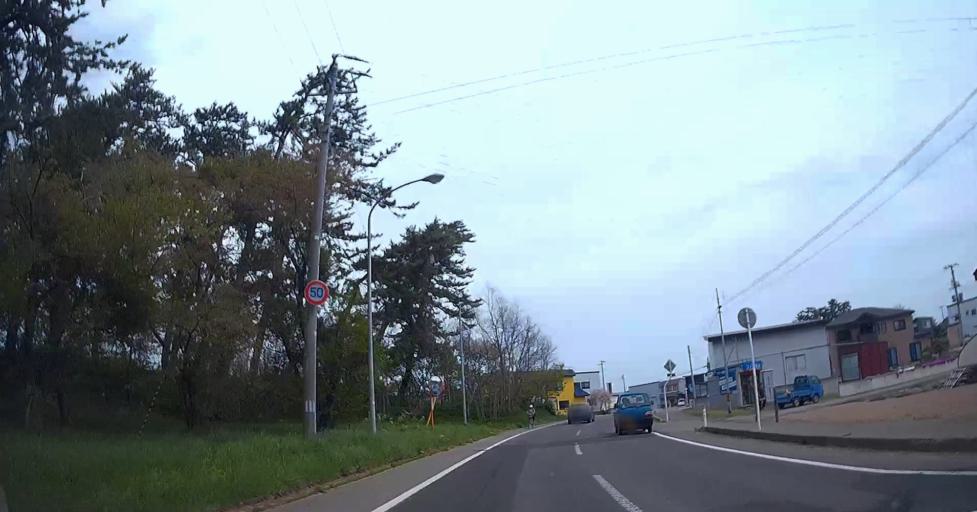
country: JP
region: Aomori
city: Shimokizukuri
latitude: 40.9698
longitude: 140.3667
